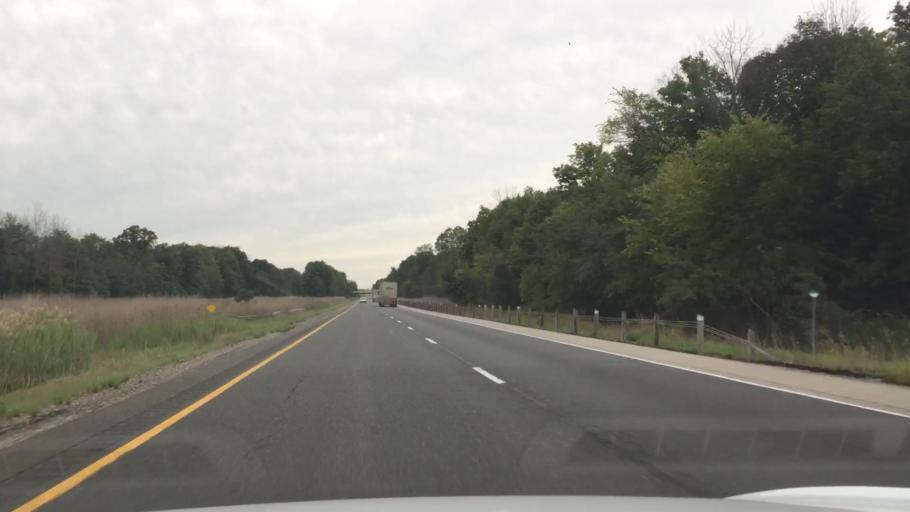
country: CA
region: Ontario
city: Lambton Shores
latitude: 42.9923
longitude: -81.7761
